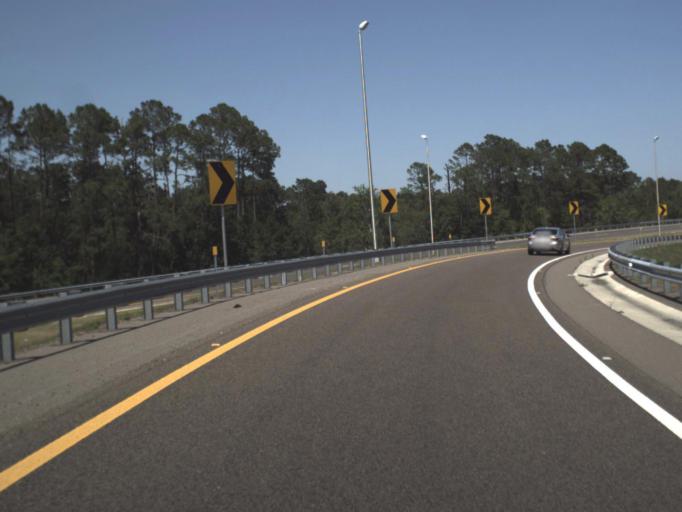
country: US
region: Florida
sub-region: Duval County
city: Baldwin
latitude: 30.3097
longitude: -81.8777
